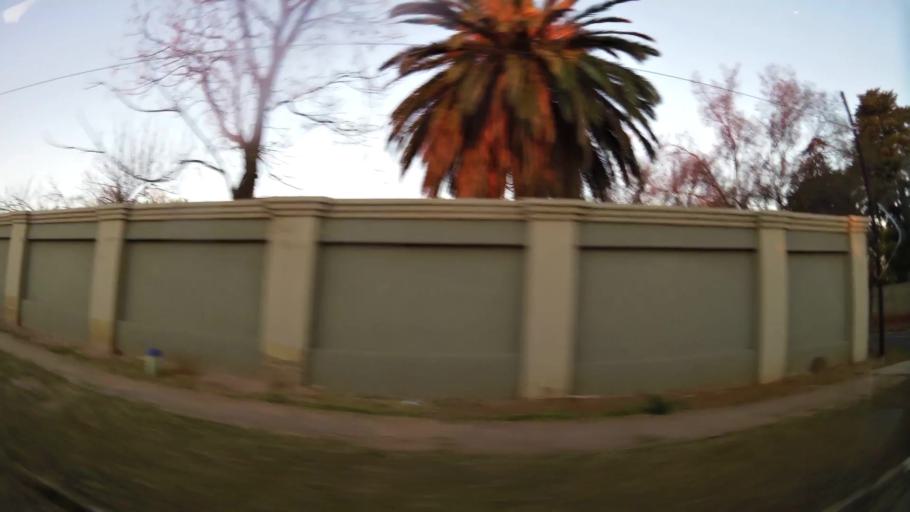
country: ZA
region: Gauteng
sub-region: City of Johannesburg Metropolitan Municipality
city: Roodepoort
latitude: -26.1705
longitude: 27.9160
